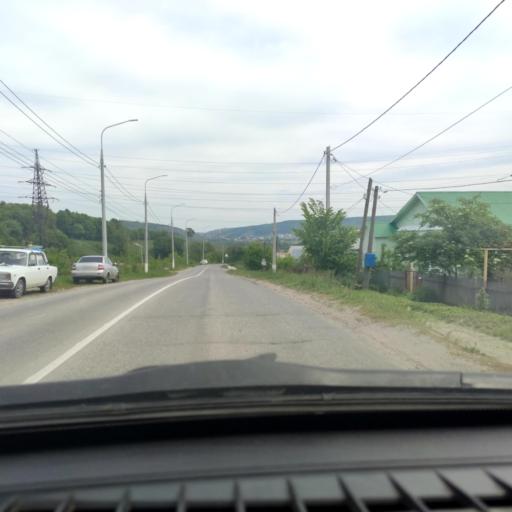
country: RU
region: Samara
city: Zhigulevsk
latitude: 53.3906
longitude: 49.4853
